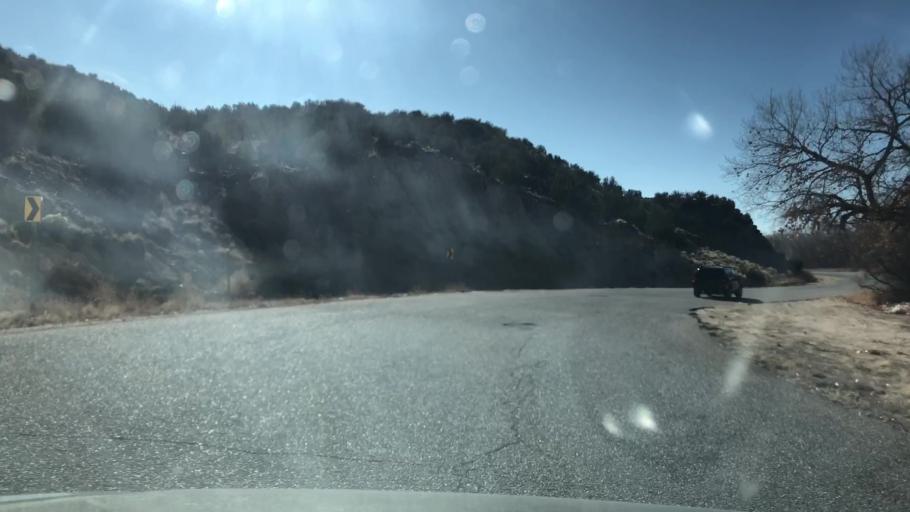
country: US
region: New Mexico
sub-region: Rio Arriba County
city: Ohkay Owingeh
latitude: 36.0957
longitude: -106.1293
